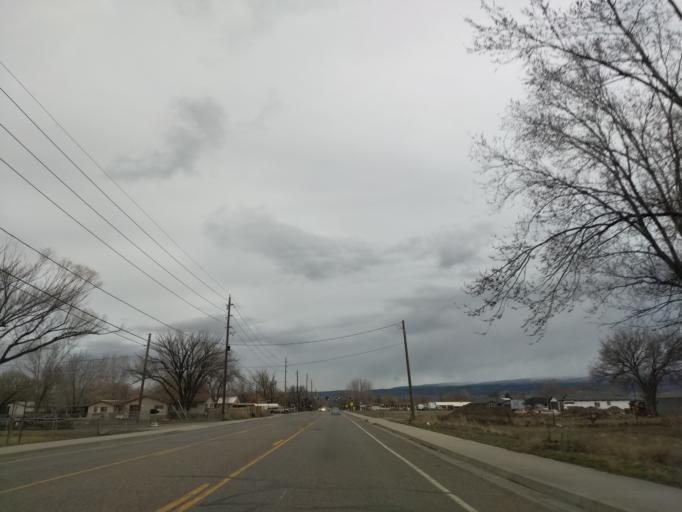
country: US
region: Colorado
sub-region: Mesa County
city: Fruitvale
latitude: 39.0726
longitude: -108.4966
